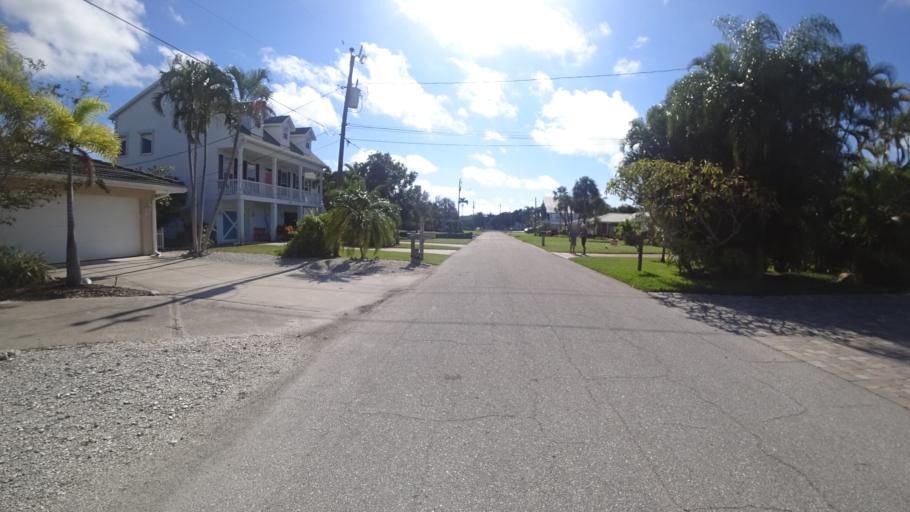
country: US
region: Florida
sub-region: Manatee County
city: Anna Maria
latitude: 27.5249
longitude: -82.7251
